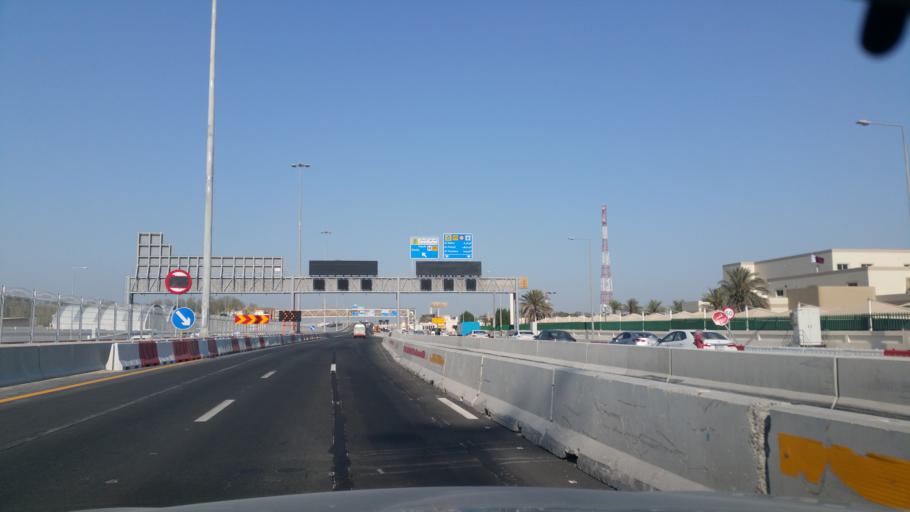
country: QA
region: Baladiyat ad Dawhah
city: Doha
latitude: 25.2319
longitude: 51.5164
